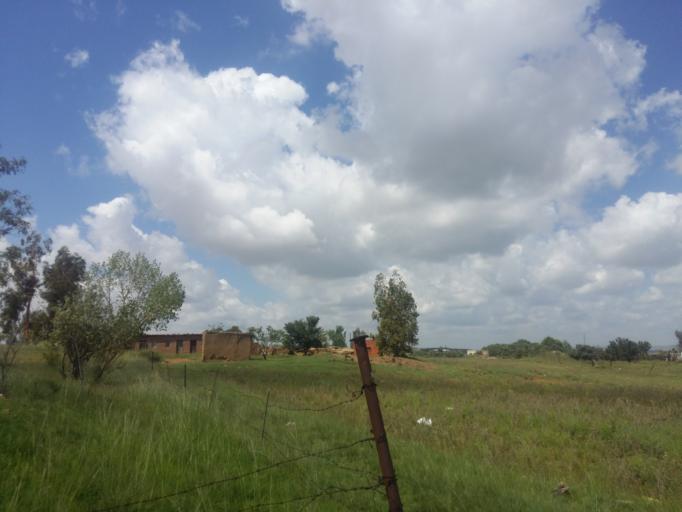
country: LS
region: Mafeteng
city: Mafeteng
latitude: -29.7530
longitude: 27.1132
